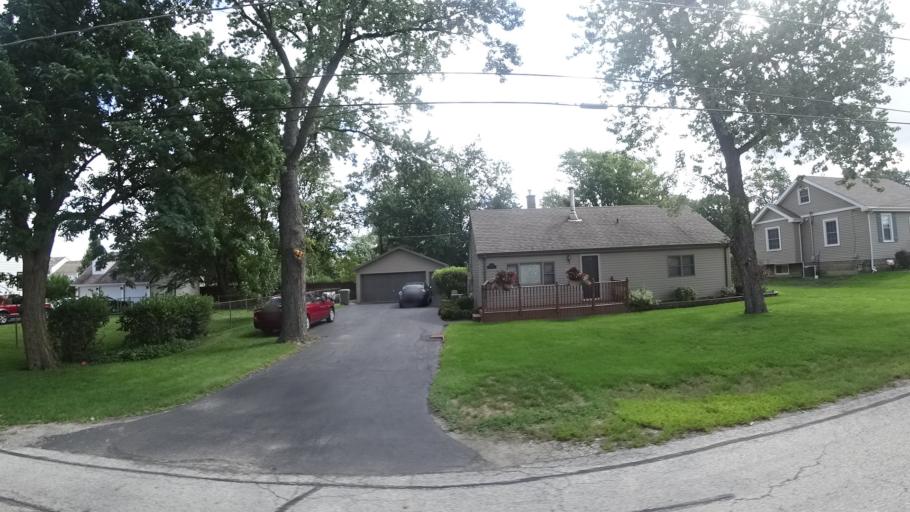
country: US
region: Illinois
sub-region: Cook County
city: Tinley Park
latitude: 41.5728
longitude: -87.7794
